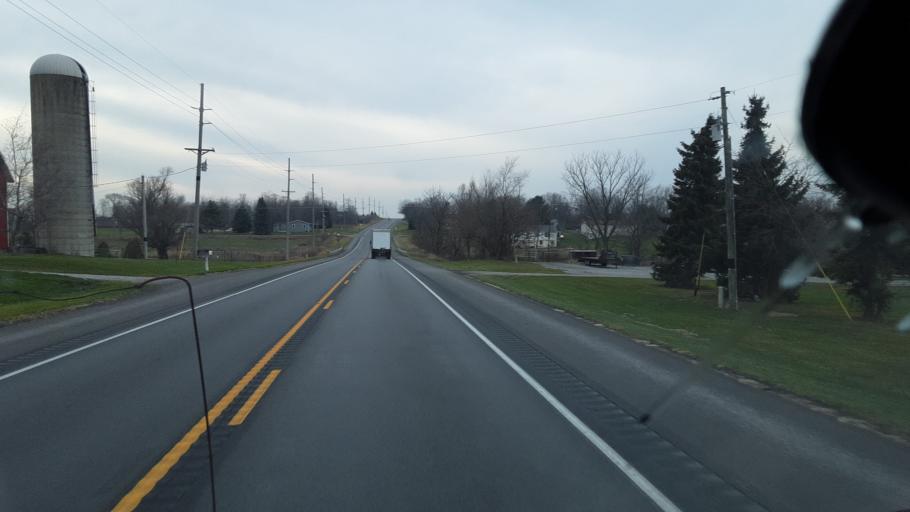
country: US
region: Indiana
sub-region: LaGrange County
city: Lagrange
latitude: 41.6419
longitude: -85.3456
